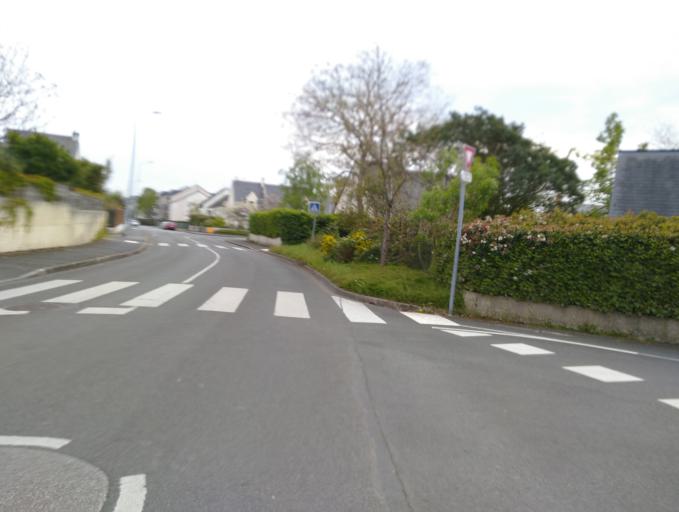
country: FR
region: Pays de la Loire
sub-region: Departement de Maine-et-Loire
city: Angers
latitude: 47.4521
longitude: -0.5306
